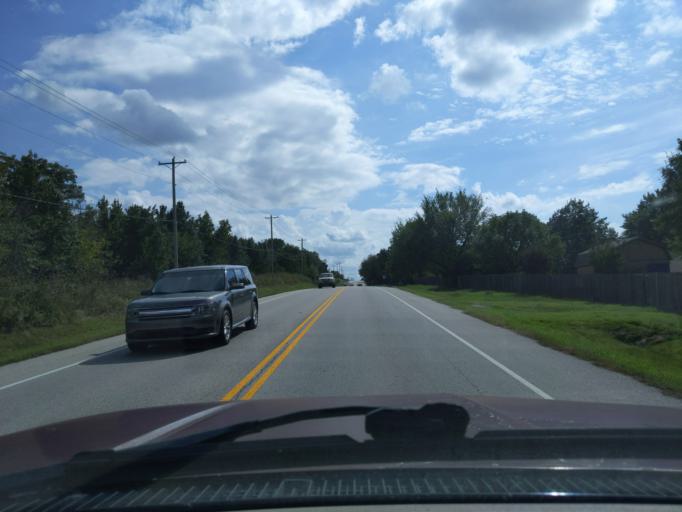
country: US
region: Oklahoma
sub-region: Tulsa County
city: Oakhurst
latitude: 36.0698
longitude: -96.0117
